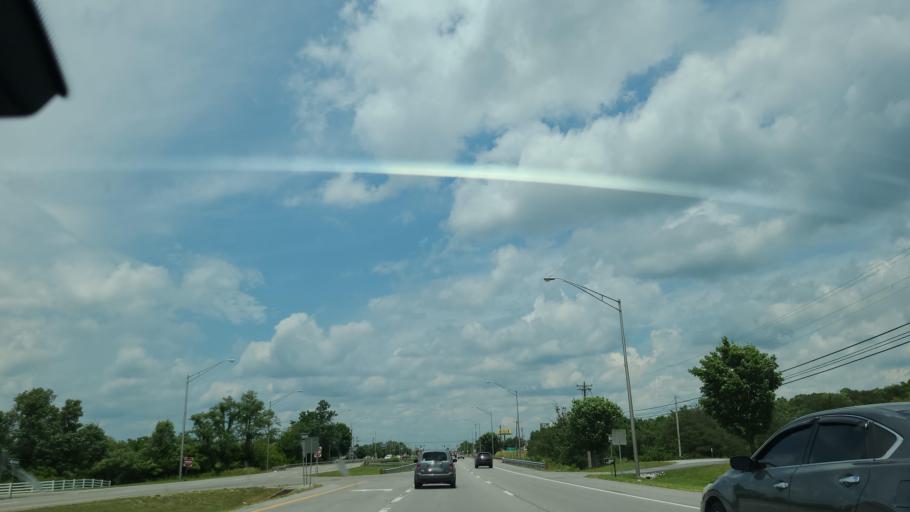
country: US
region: Tennessee
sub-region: Cumberland County
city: Crossville
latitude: 35.9747
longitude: -85.0382
